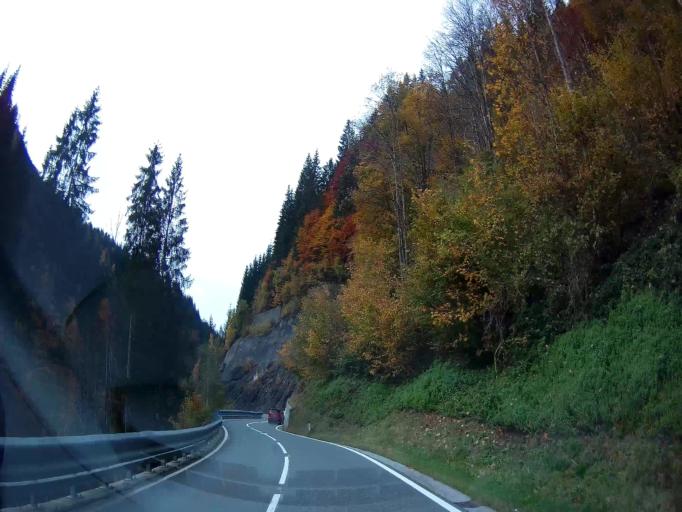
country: AT
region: Salzburg
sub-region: Politischer Bezirk Sankt Johann im Pongau
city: Bischofshofen
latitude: 47.3966
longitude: 13.1908
